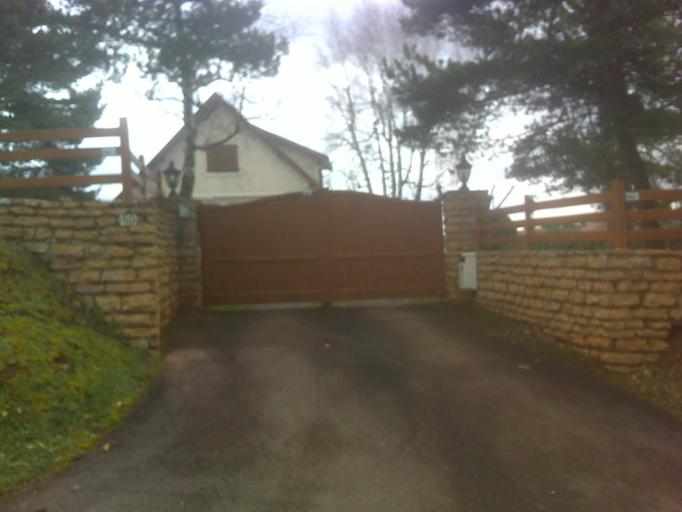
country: FR
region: Rhone-Alpes
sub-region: Departement du Rhone
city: Lentilly
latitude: 45.8166
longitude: 4.6519
